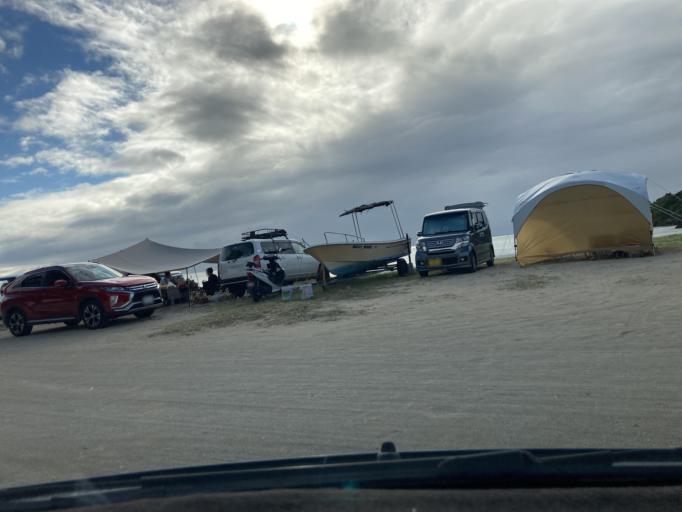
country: JP
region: Okinawa
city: Itoman
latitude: 26.1082
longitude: 127.6618
